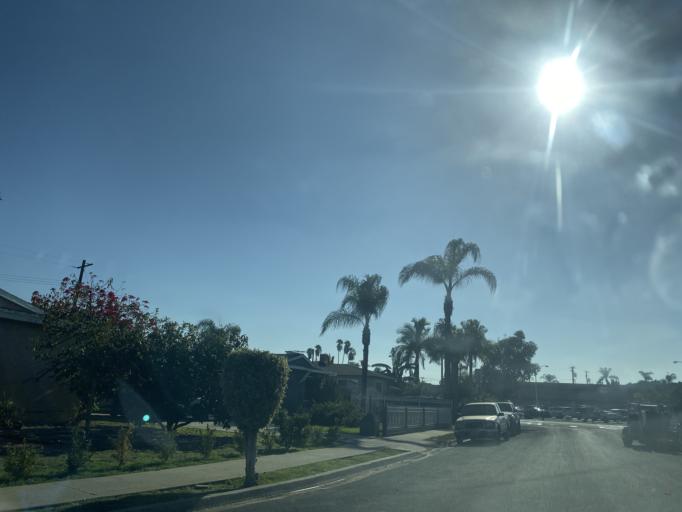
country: US
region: California
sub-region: Orange County
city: Placentia
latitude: 33.8742
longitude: -117.8772
